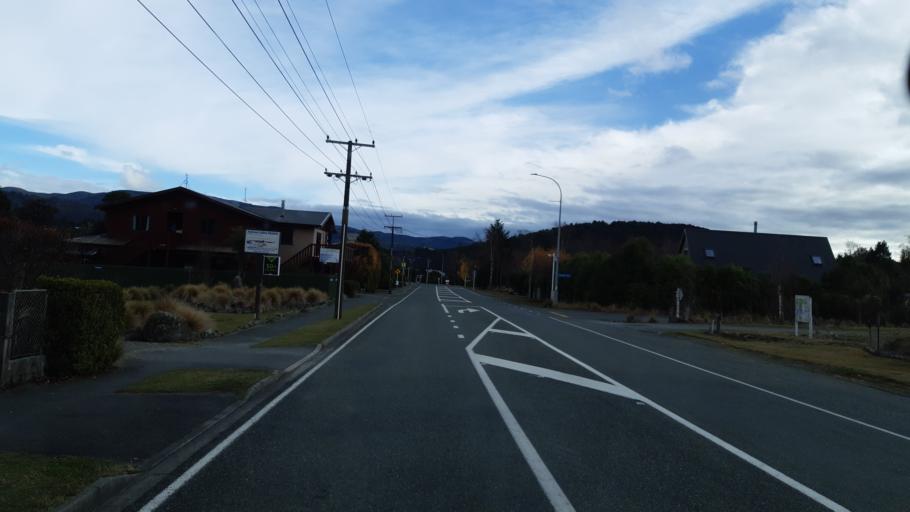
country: NZ
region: Tasman
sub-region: Tasman District
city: Wakefield
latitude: -41.8014
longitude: 172.8519
